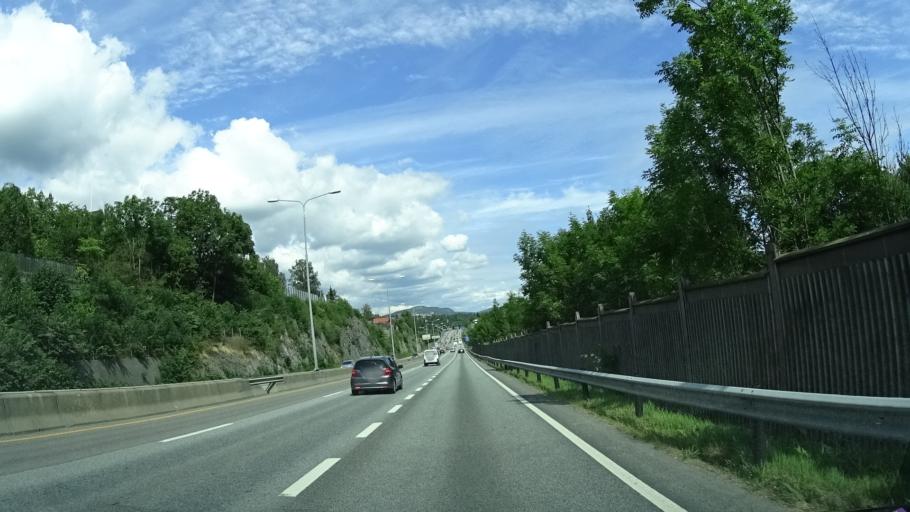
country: NO
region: Akershus
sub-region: Asker
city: Billingstad
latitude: 59.8616
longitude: 10.4859
